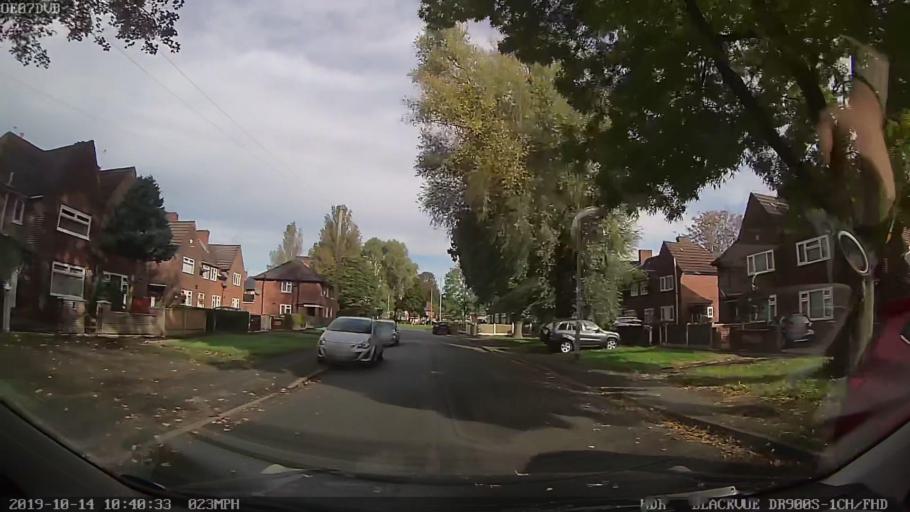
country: GB
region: England
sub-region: Manchester
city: Blackley
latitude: 53.5248
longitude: -2.1924
